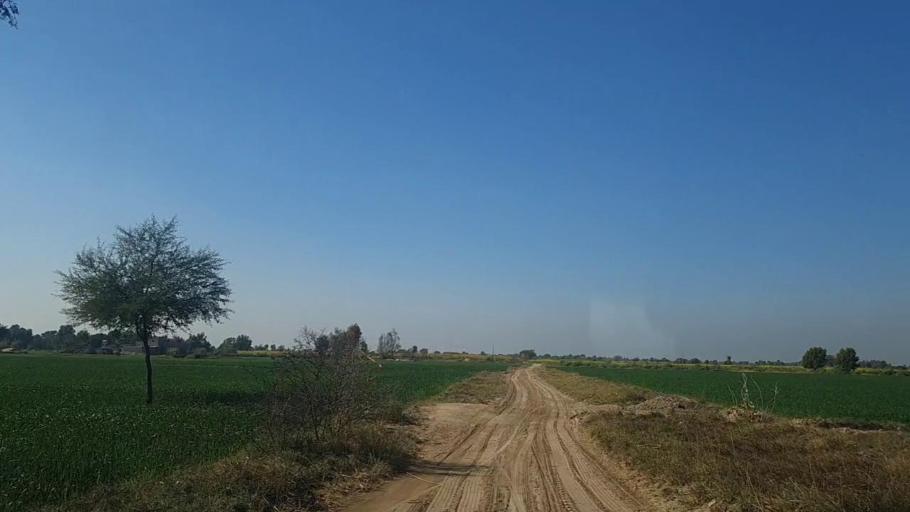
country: PK
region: Sindh
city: Sinjhoro
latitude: 26.1308
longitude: 68.8437
